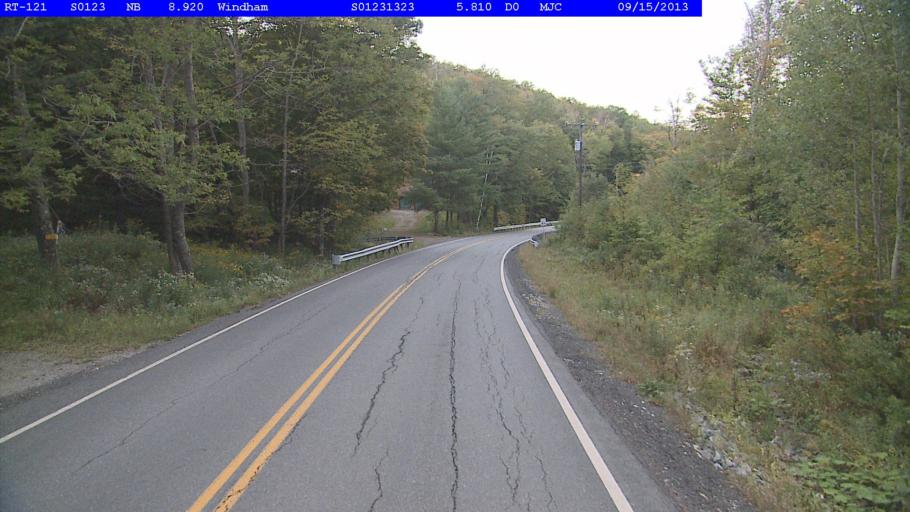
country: US
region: Vermont
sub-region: Windsor County
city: Chester
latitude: 43.2002
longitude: -72.7311
